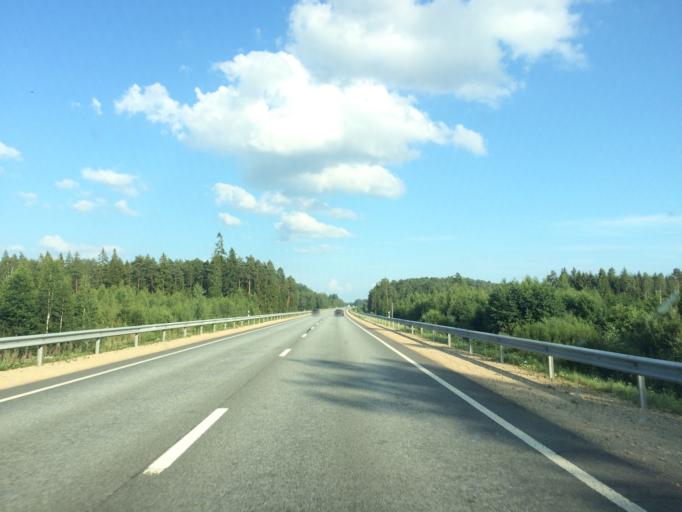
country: LV
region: Skriveri
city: Skriveri
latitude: 56.7208
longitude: 25.1950
